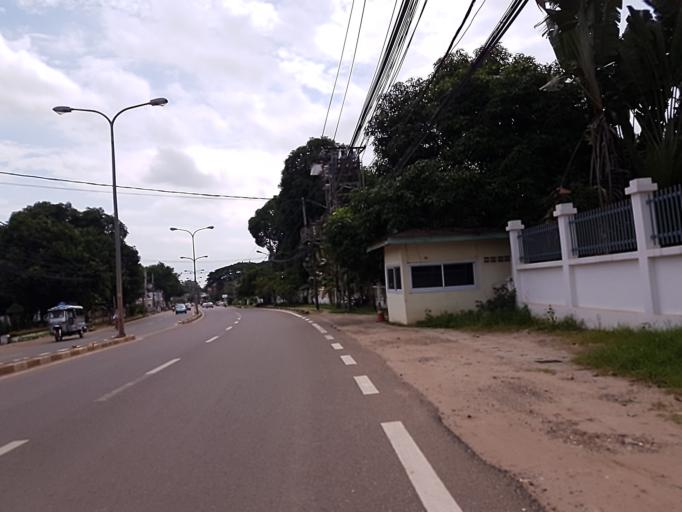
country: LA
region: Vientiane
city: Vientiane
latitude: 17.9342
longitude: 102.6166
